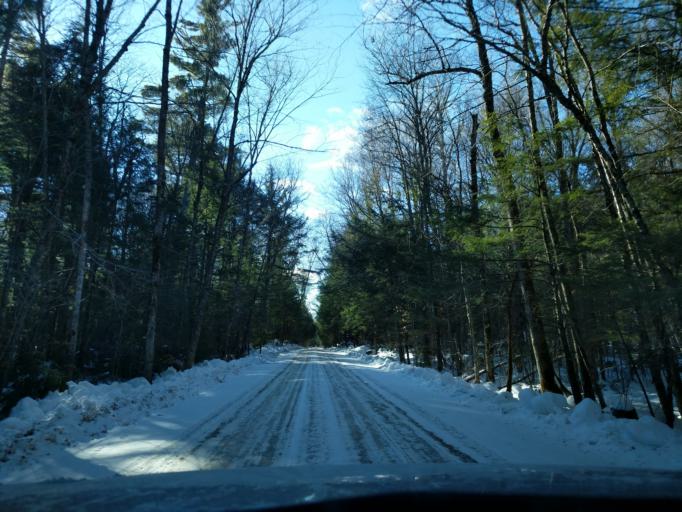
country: US
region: Wisconsin
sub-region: Menominee County
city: Keshena
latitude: 45.0960
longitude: -88.6150
